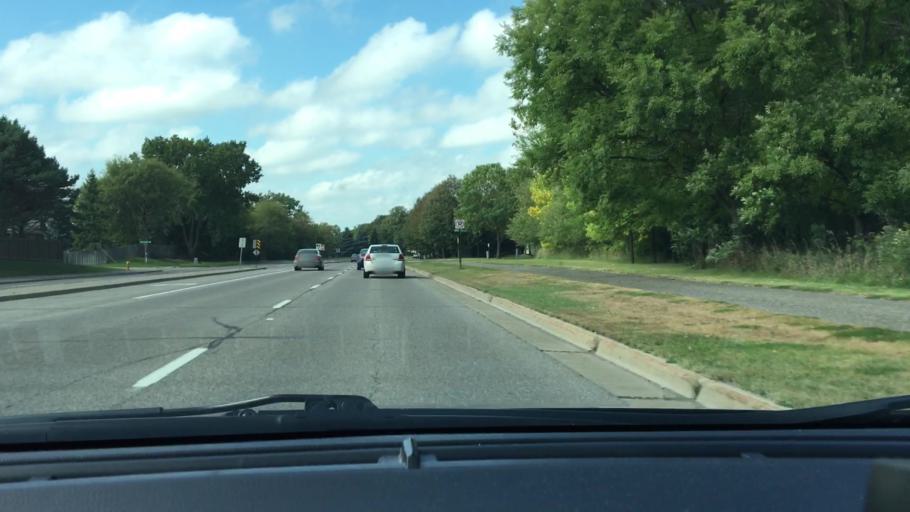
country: US
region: Minnesota
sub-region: Hennepin County
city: Maple Grove
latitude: 45.0585
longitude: -93.4245
